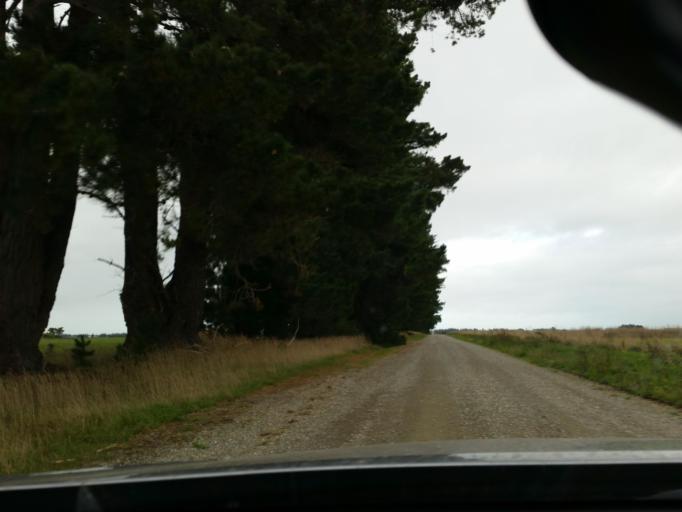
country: NZ
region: Southland
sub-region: Southland District
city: Winton
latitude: -46.2052
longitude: 168.3671
